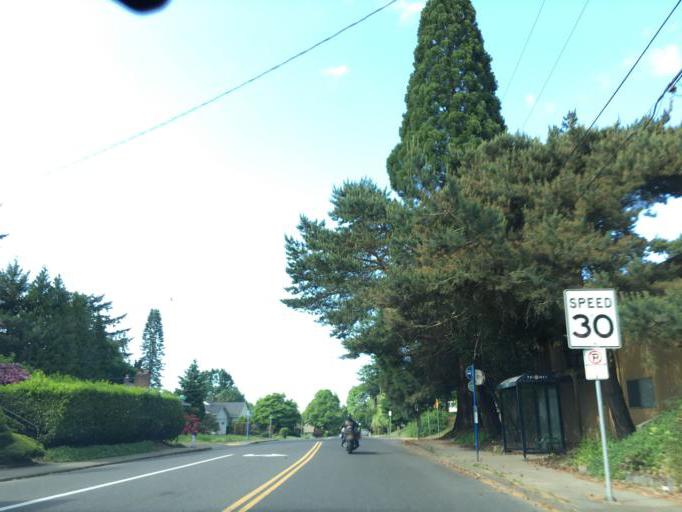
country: US
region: Oregon
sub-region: Clackamas County
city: Milwaukie
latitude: 45.4795
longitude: -122.6226
